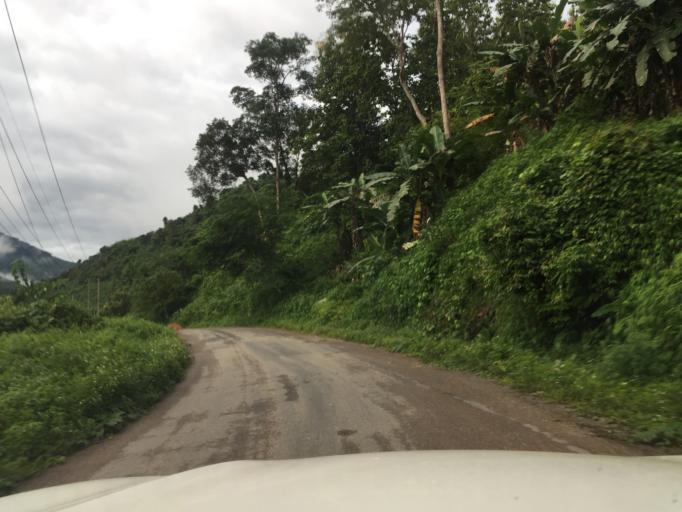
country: LA
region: Oudomxai
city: Muang La
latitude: 21.0653
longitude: 102.2398
